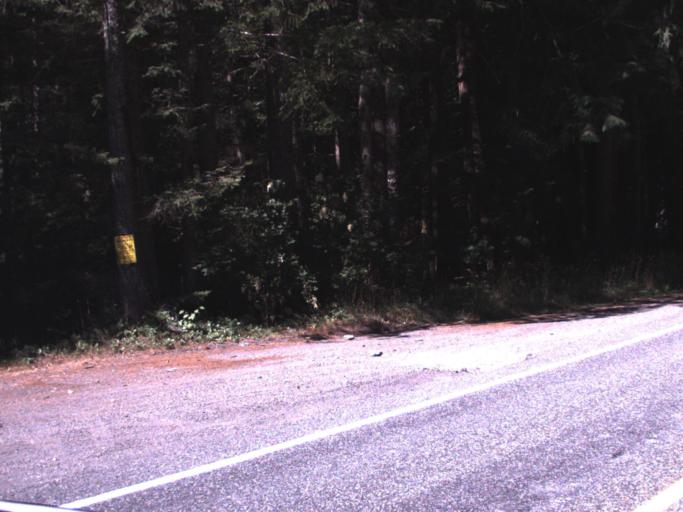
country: US
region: Washington
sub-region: King County
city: Enumclaw
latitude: 47.1708
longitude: -121.7689
